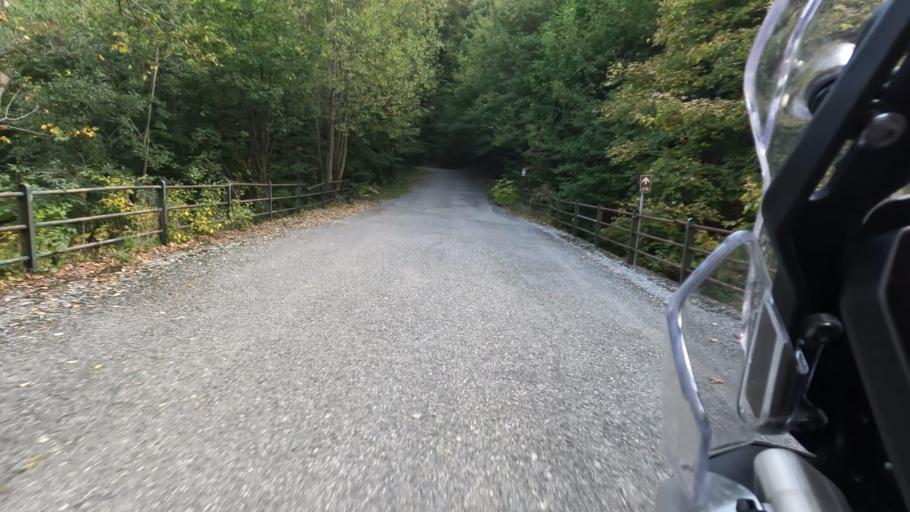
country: IT
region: Liguria
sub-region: Provincia di Savona
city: Urbe
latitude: 44.4426
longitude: 8.5775
